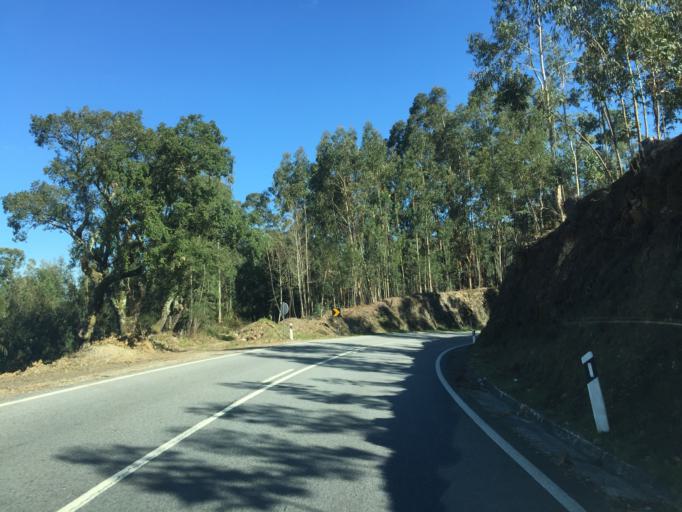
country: PT
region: Aveiro
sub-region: Vale de Cambra
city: Macieira de Cambra
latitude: 40.9027
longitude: -8.3308
